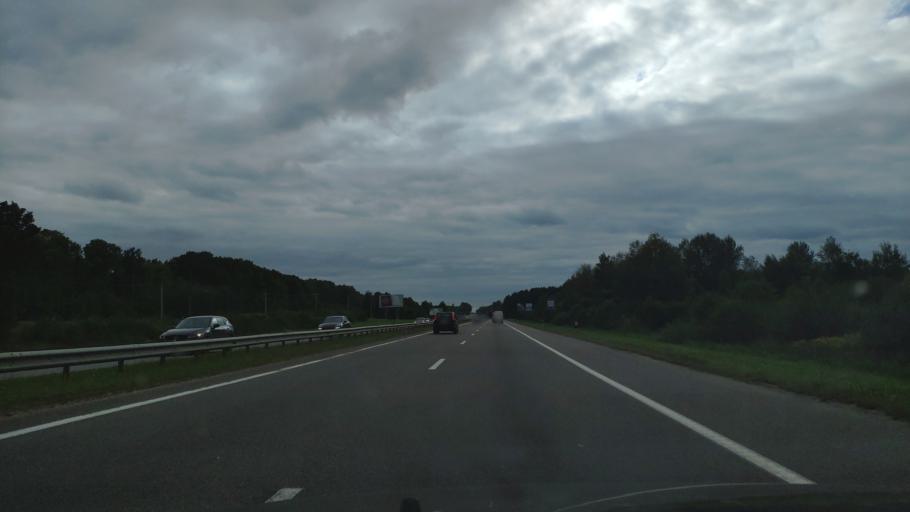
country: BY
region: Minsk
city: Zhdanovichy
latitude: 53.9515
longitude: 27.3948
